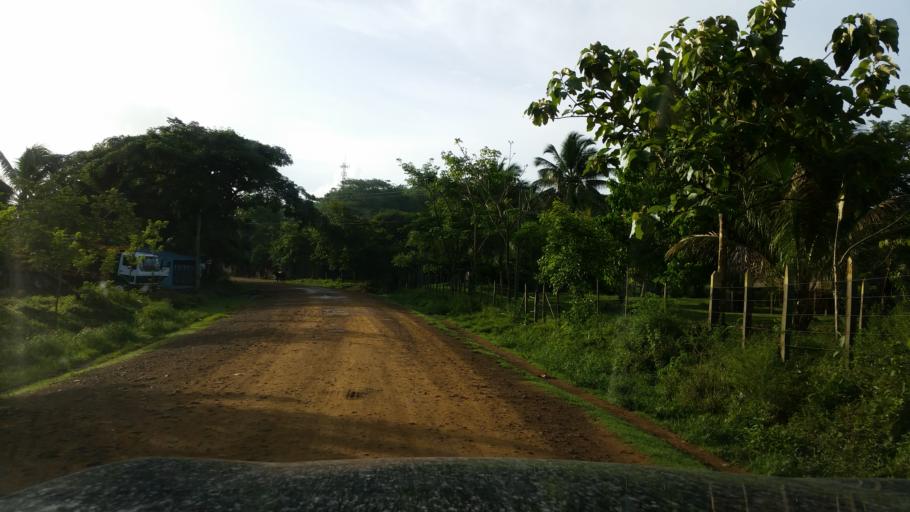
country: NI
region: Atlantico Norte (RAAN)
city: Puerto Cabezas
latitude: 14.0676
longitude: -83.9861
